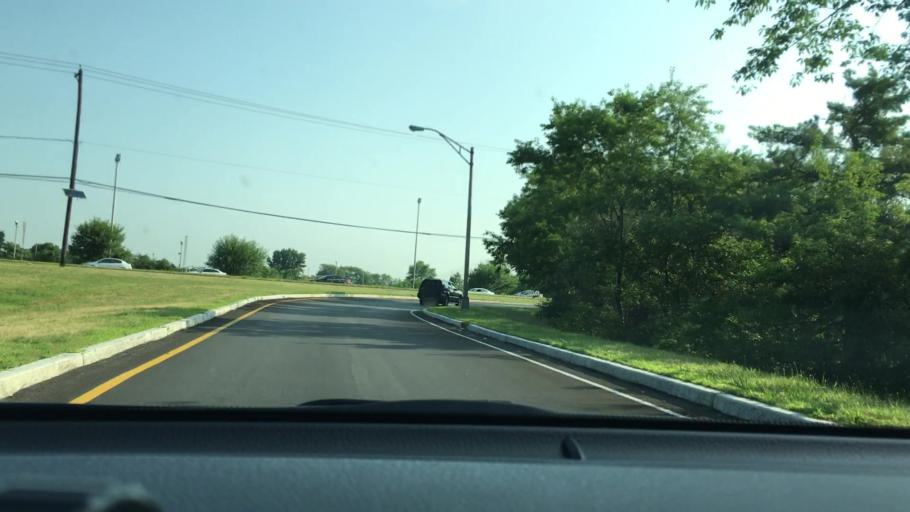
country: US
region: New Jersey
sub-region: Burlington County
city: Mount Laurel
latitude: 39.9666
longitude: -74.9097
